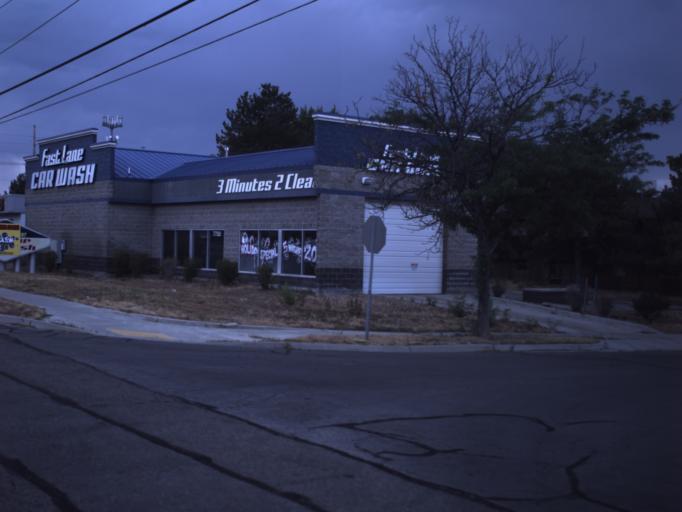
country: US
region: Utah
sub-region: Salt Lake County
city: Sandy City
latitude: 40.6106
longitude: -111.8723
